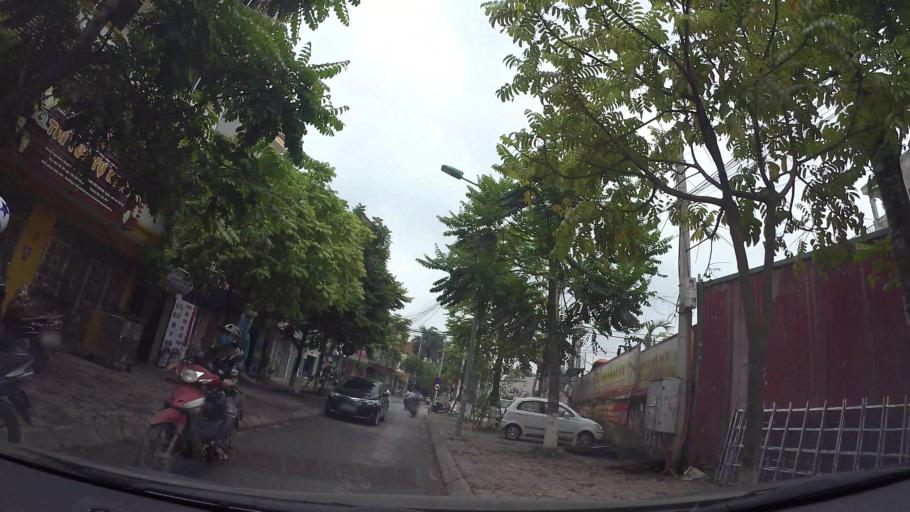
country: VN
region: Ha Noi
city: Van Dien
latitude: 20.9738
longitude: 105.8486
